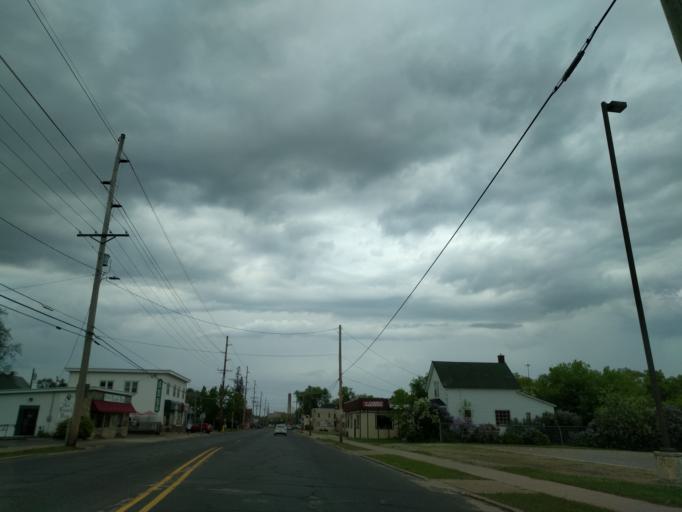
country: US
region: Michigan
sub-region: Marquette County
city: Marquette
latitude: 46.5595
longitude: -87.3961
